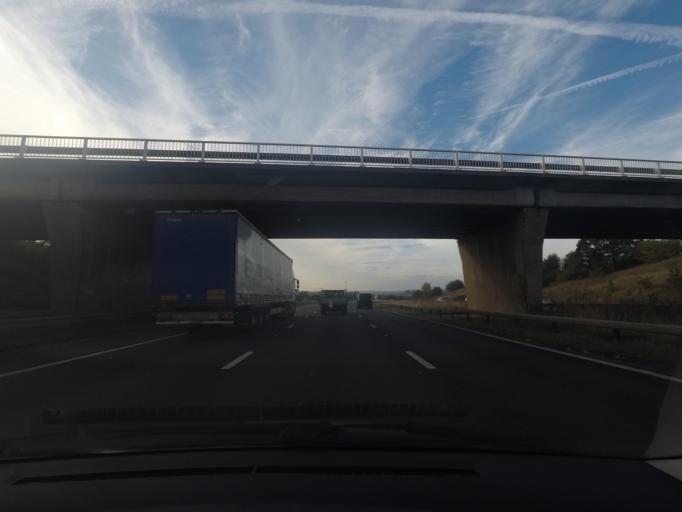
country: GB
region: England
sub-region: Barnsley
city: Darton
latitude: 53.5799
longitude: -1.5372
